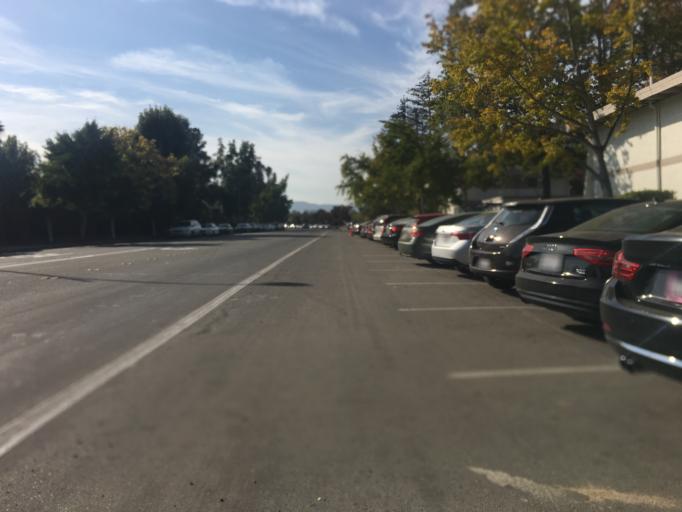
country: US
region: California
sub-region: Santa Clara County
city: Cupertino
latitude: 37.3289
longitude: -122.0506
